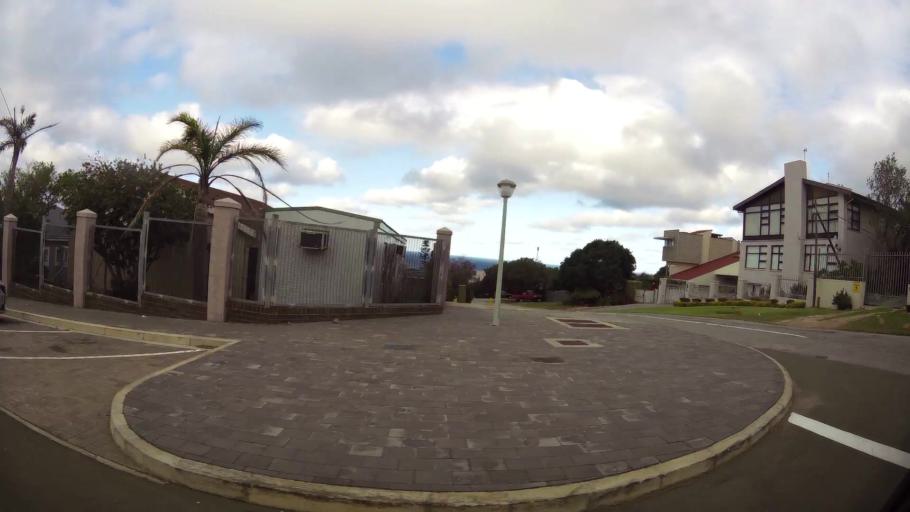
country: ZA
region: Western Cape
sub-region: Eden District Municipality
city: Plettenberg Bay
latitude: -34.0579
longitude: 23.3716
